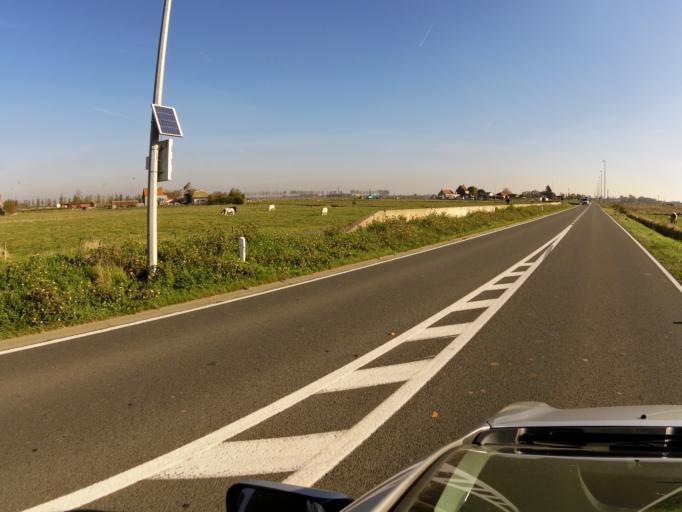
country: BE
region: Flanders
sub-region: Provincie West-Vlaanderen
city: Middelkerke
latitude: 51.1519
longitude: 2.8463
